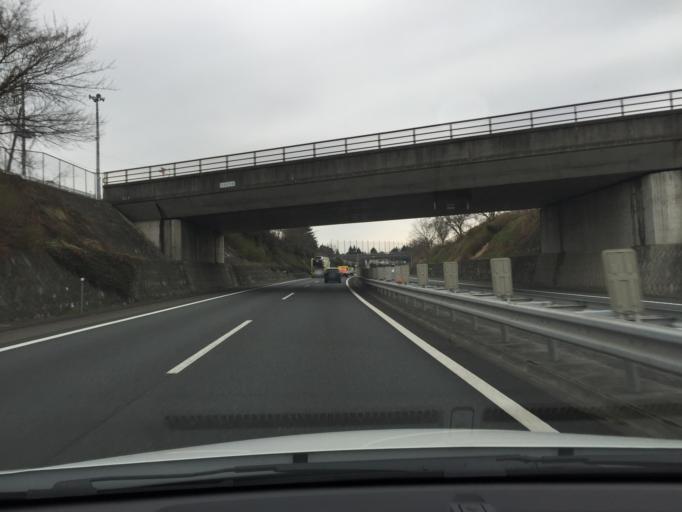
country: JP
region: Saitama
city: Hanno
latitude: 35.8104
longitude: 139.3566
